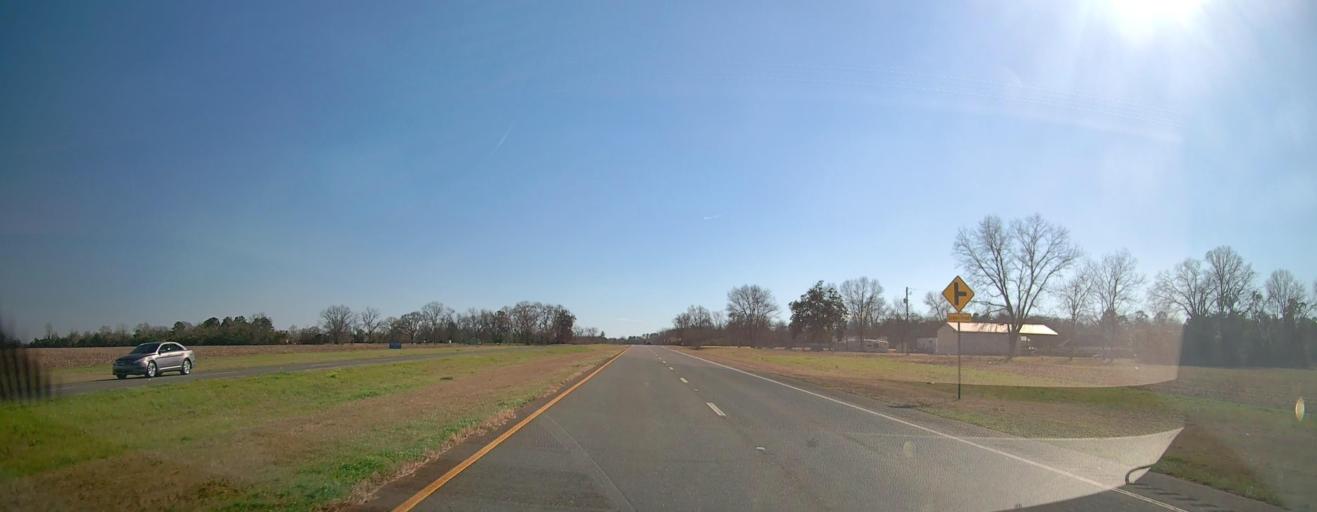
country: US
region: Georgia
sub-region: Schley County
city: Ellaville
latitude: 32.1694
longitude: -84.2692
